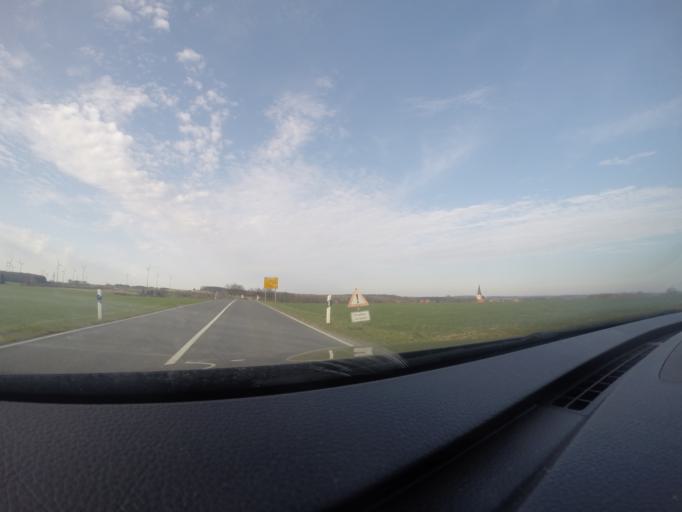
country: DE
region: North Rhine-Westphalia
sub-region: Regierungsbezirk Munster
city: Horstmar
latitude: 52.0743
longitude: 7.2938
